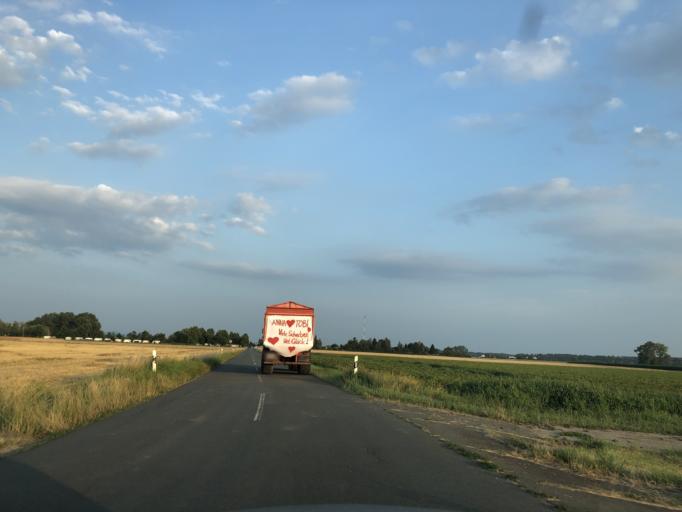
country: DE
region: Rheinland-Pfalz
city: Nierstein
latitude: 49.8821
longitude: 8.3754
